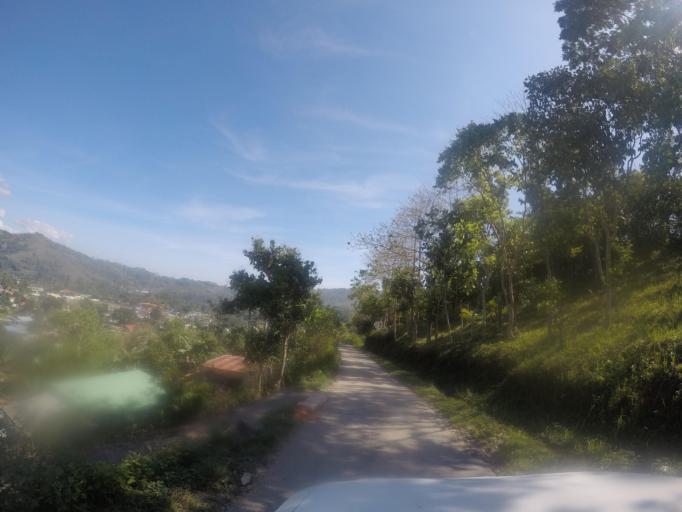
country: TL
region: Ermera
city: Gleno
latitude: -8.7274
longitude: 125.4373
